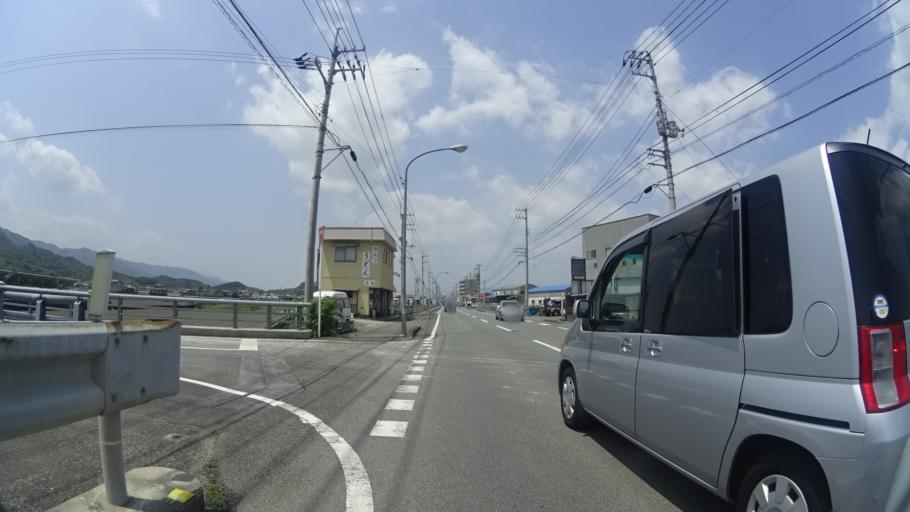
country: JP
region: Tokushima
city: Ishii
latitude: 34.0695
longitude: 134.4079
